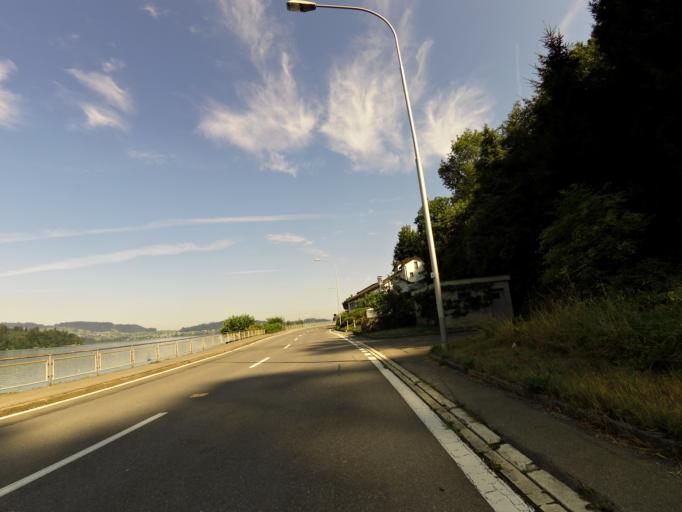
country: CH
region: Zug
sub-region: Zug
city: Walchwil
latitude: 47.1112
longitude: 8.5023
